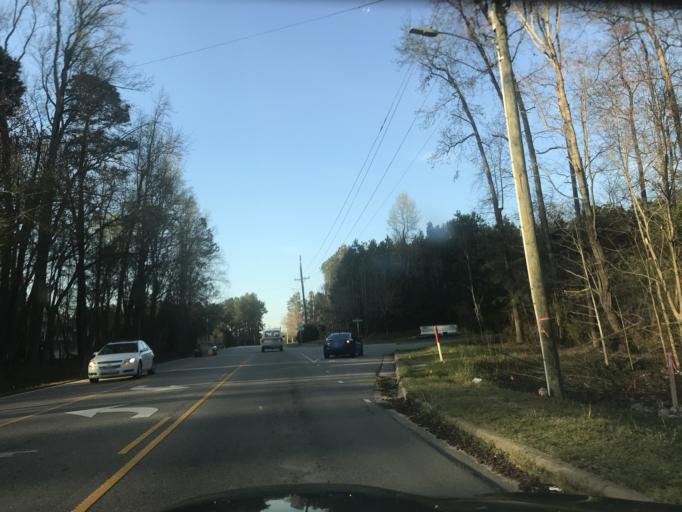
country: US
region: North Carolina
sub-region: Wake County
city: Garner
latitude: 35.7306
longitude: -78.5559
